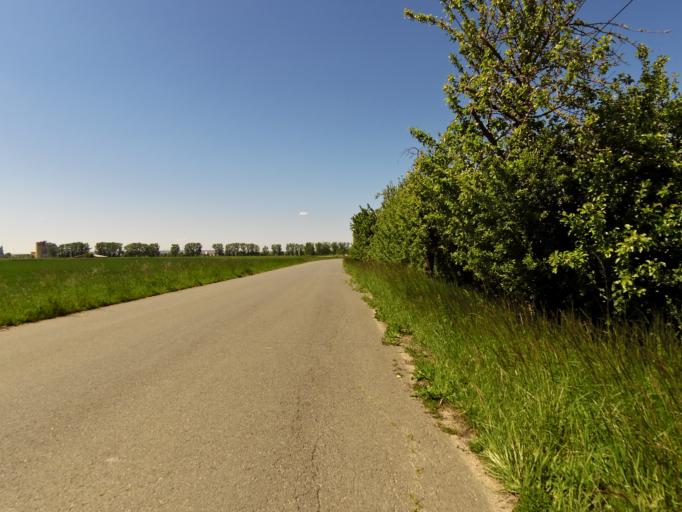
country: DE
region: Rheinland-Pfalz
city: Osthofen
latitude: 49.6888
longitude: 8.3761
